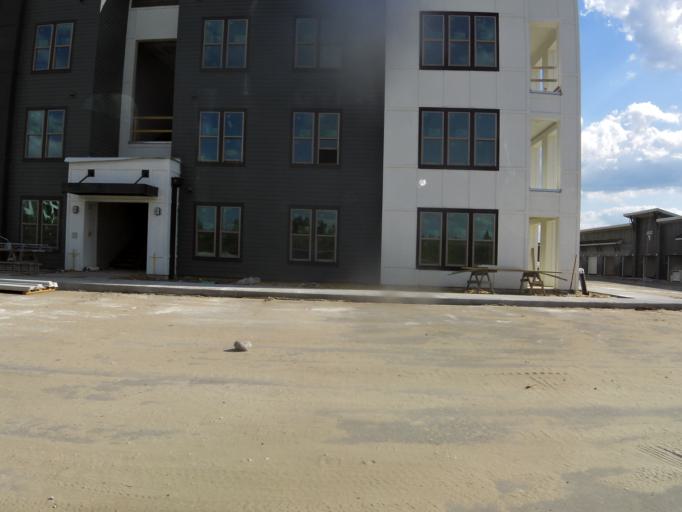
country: US
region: Florida
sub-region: Saint Johns County
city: Palm Valley
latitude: 30.1638
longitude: -81.5092
